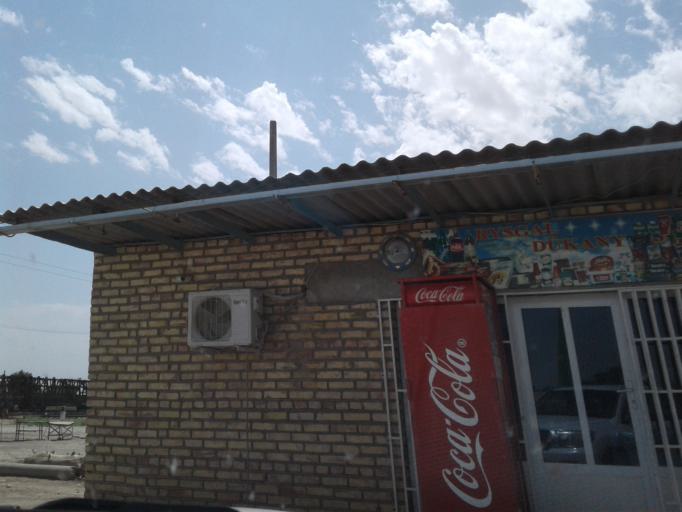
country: IR
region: Razavi Khorasan
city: Kalat-e Naderi
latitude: 37.2004
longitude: 60.0291
